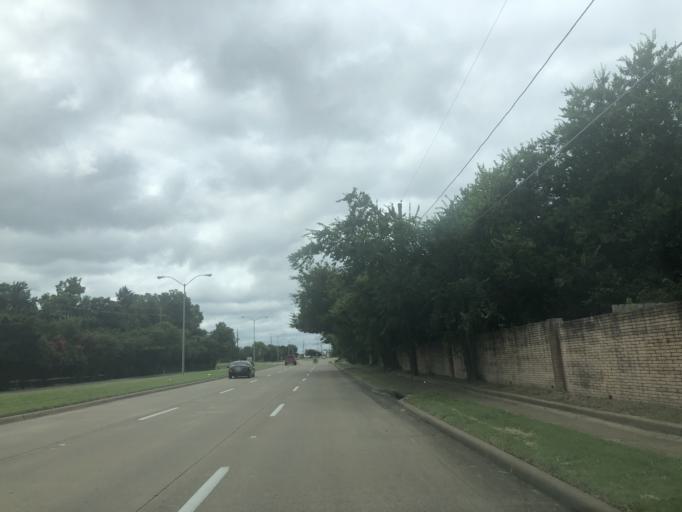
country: US
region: Texas
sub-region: Dallas County
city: Duncanville
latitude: 32.6371
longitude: -96.9430
